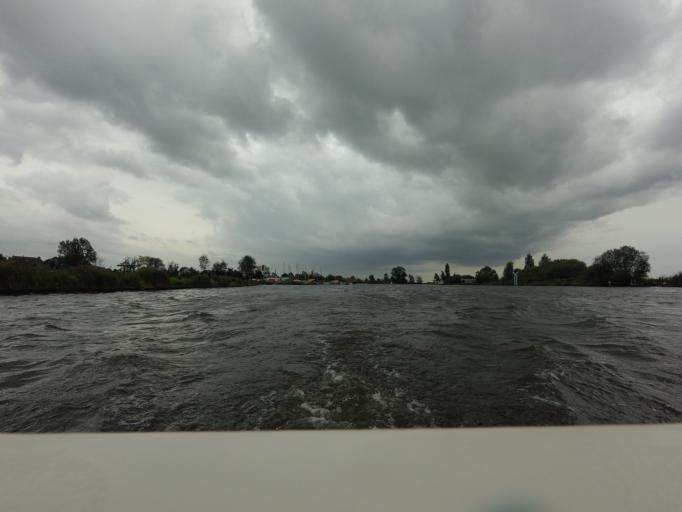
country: NL
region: Friesland
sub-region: Gemeente Smallingerland
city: Oudega
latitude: 53.1003
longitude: 5.9473
